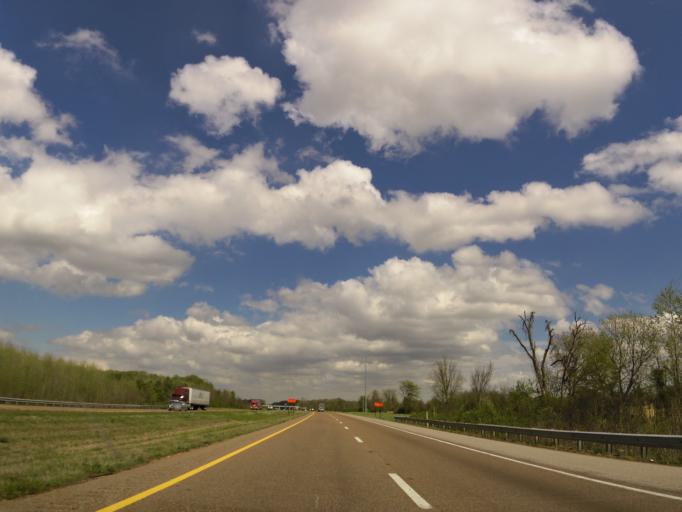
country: US
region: Tennessee
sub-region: Shelby County
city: Arlington
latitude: 35.2864
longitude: -89.6185
